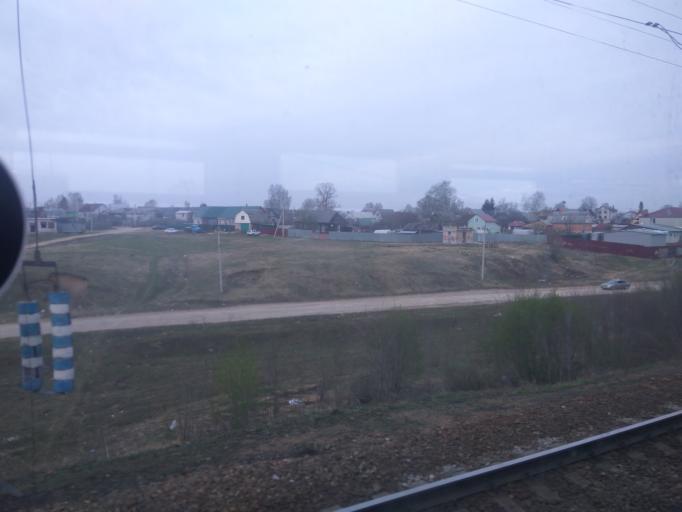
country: RU
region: Vladimir
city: Strunino
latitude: 56.3780
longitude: 38.5949
